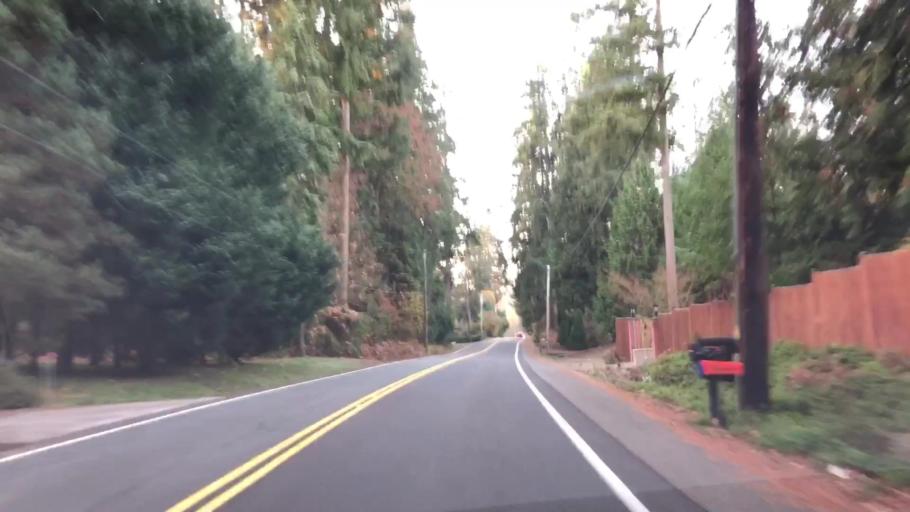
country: US
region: Washington
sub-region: King County
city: Cottage Lake
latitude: 47.7267
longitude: -122.0759
